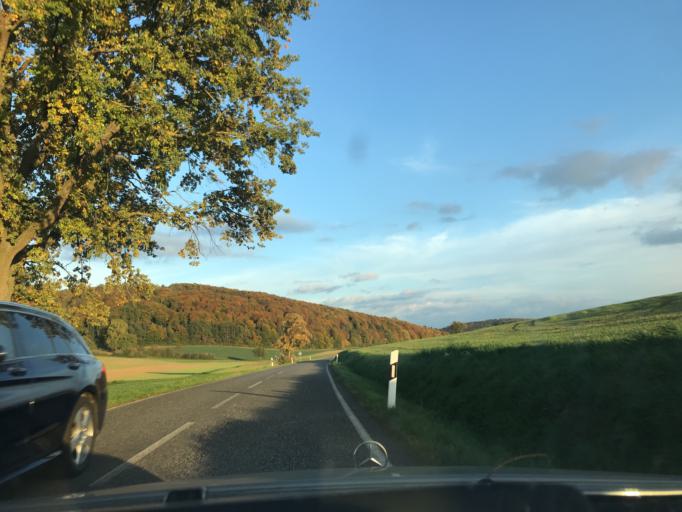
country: DE
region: Hesse
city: Witzenhausen
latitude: 51.4087
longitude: 9.8543
